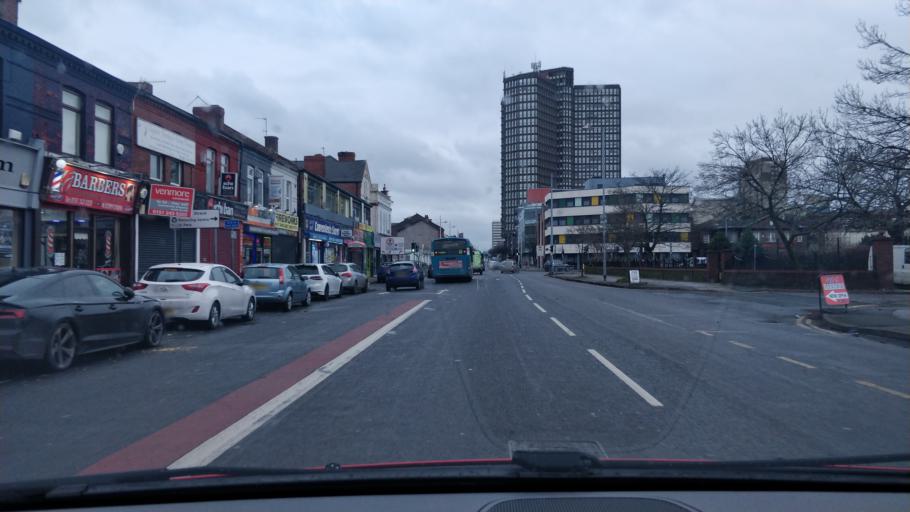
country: GB
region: England
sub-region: Sefton
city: Litherland
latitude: 53.4554
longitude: -2.9916
